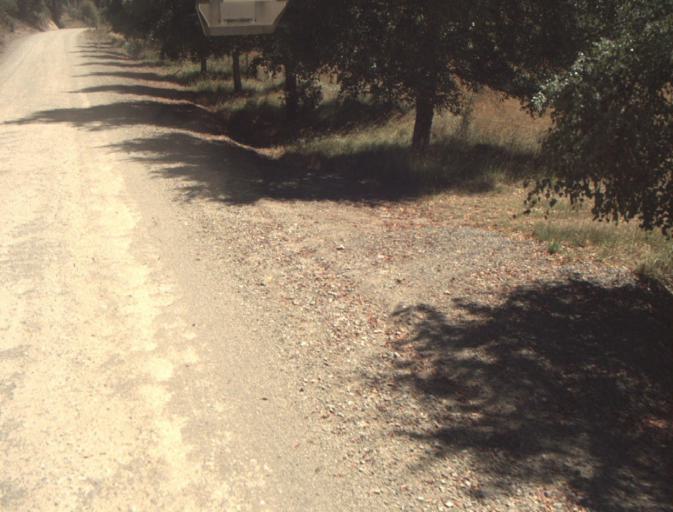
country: AU
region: Tasmania
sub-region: Dorset
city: Scottsdale
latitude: -41.2947
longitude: 147.4014
